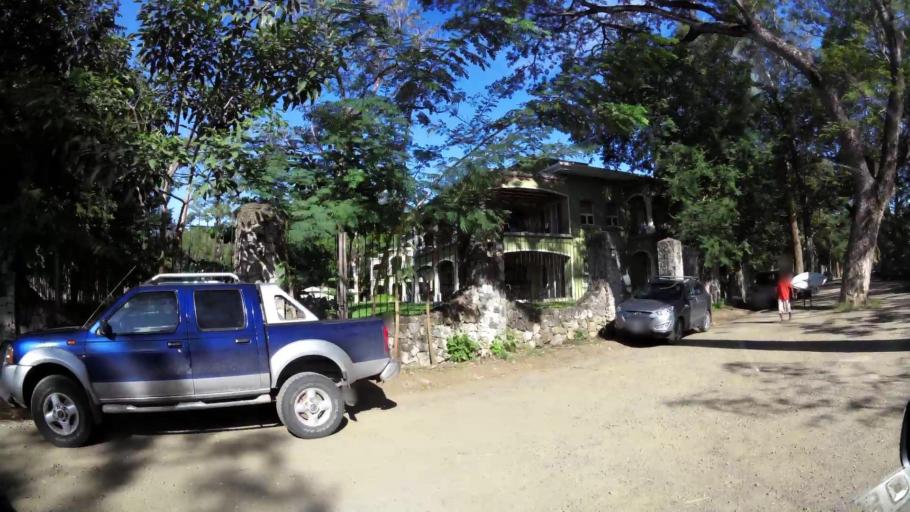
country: CR
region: Guanacaste
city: Sardinal
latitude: 10.5903
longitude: -85.6506
